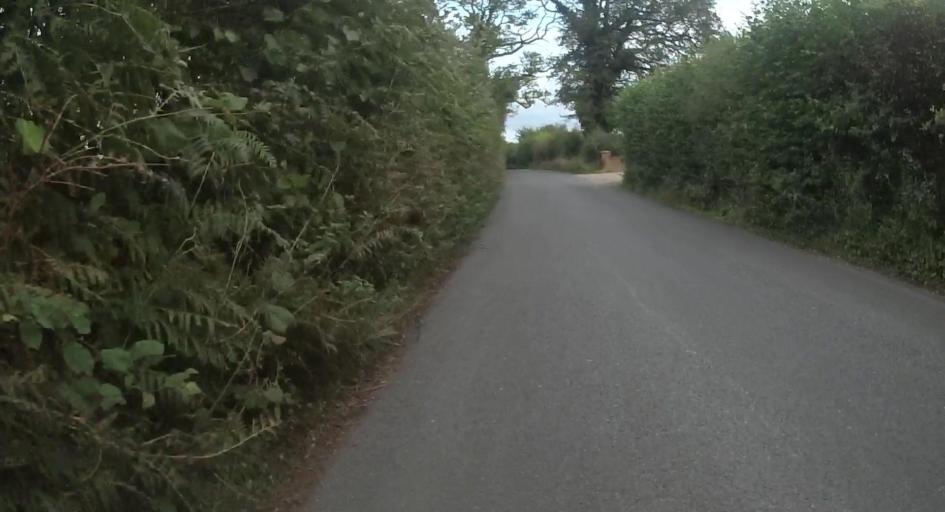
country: GB
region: England
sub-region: Hampshire
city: Odiham
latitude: 51.2916
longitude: -0.8983
